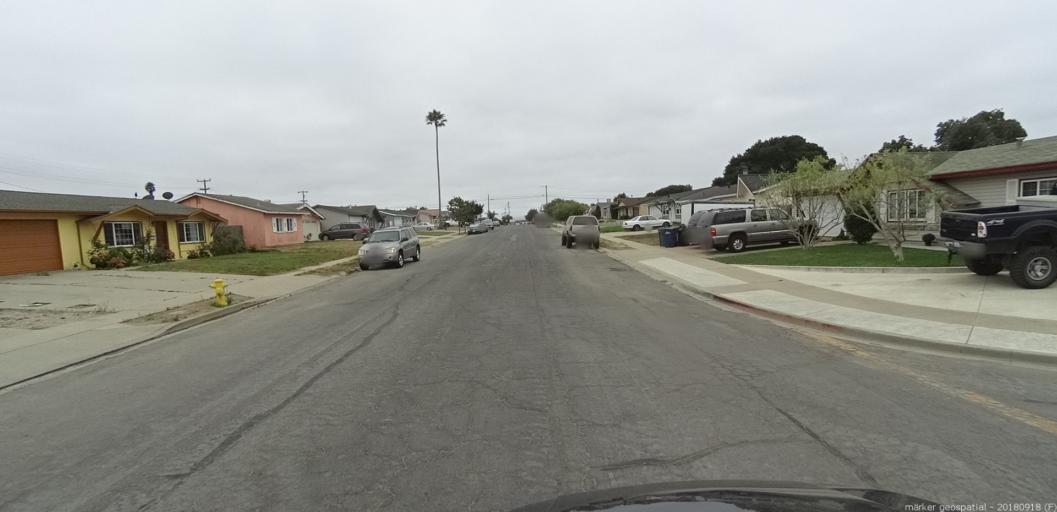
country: US
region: California
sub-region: Monterey County
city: Boronda
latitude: 36.7329
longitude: -121.6374
